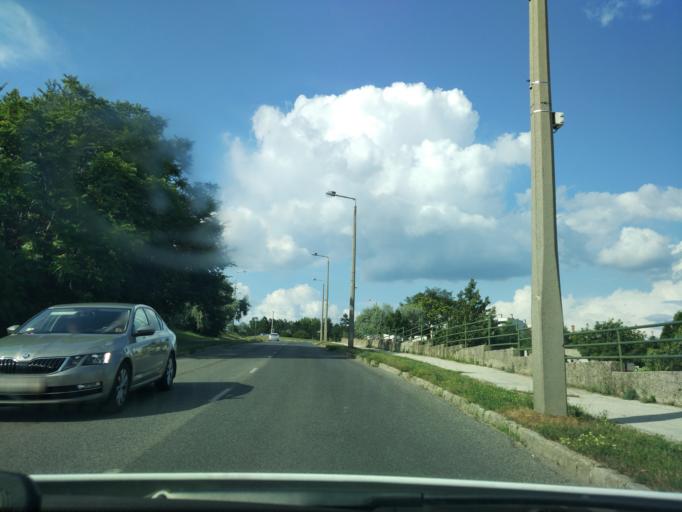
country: HU
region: Veszprem
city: Varpalota
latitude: 47.2033
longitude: 18.1481
